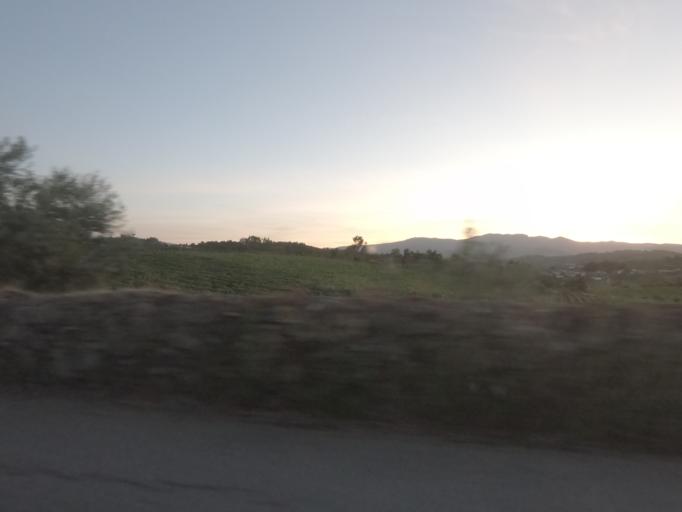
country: PT
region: Vila Real
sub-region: Peso da Regua
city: Peso da Regua
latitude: 41.1964
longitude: -7.7056
